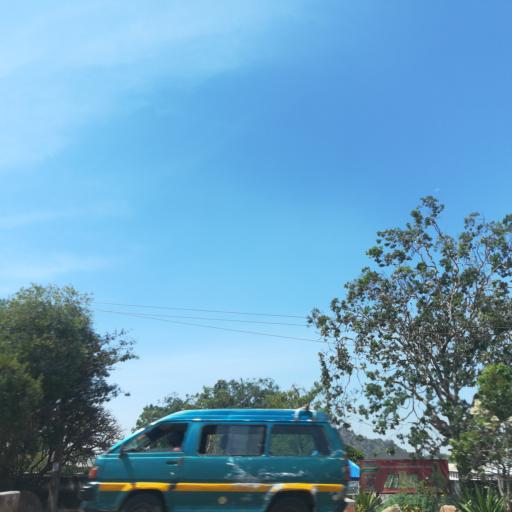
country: NG
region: Plateau
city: Bukuru
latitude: 9.8055
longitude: 8.8677
